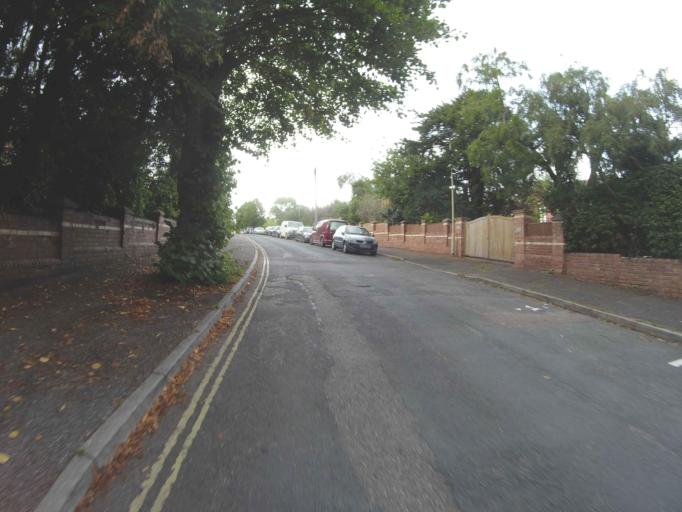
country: GB
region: England
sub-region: Devon
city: Exmouth
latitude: 50.6169
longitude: -3.4030
